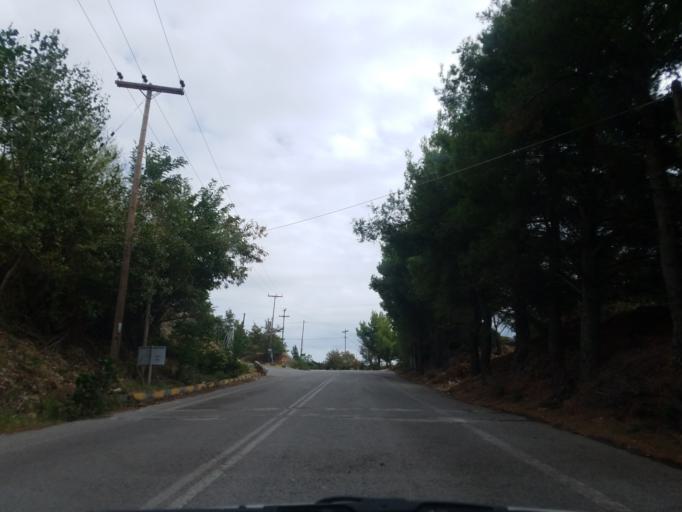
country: GR
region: Central Greece
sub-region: Nomos Voiotias
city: Arachova
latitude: 38.4839
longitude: 22.5719
